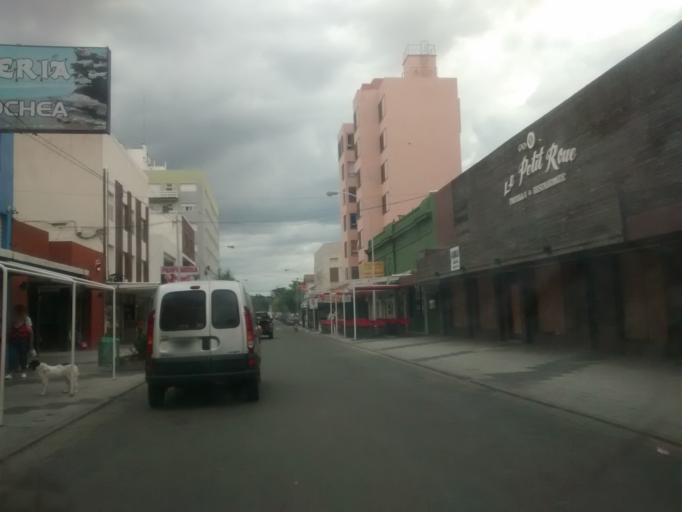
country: AR
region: Buenos Aires
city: Necochea
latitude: -38.5821
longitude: -58.7299
